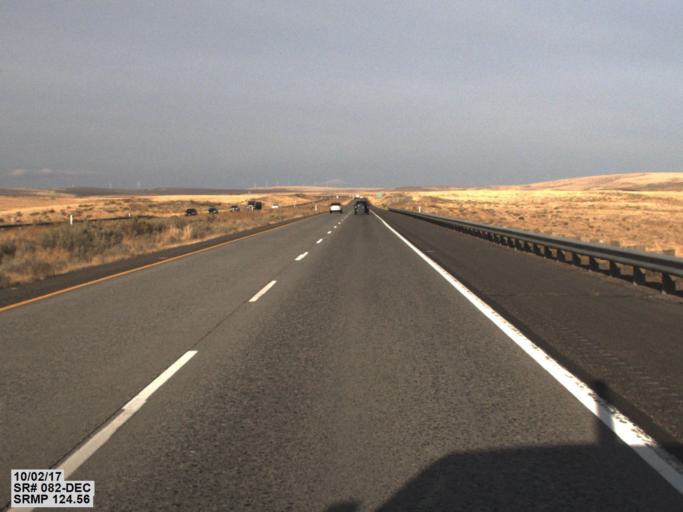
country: US
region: Oregon
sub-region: Umatilla County
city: Umatilla
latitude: 46.0055
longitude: -119.2455
